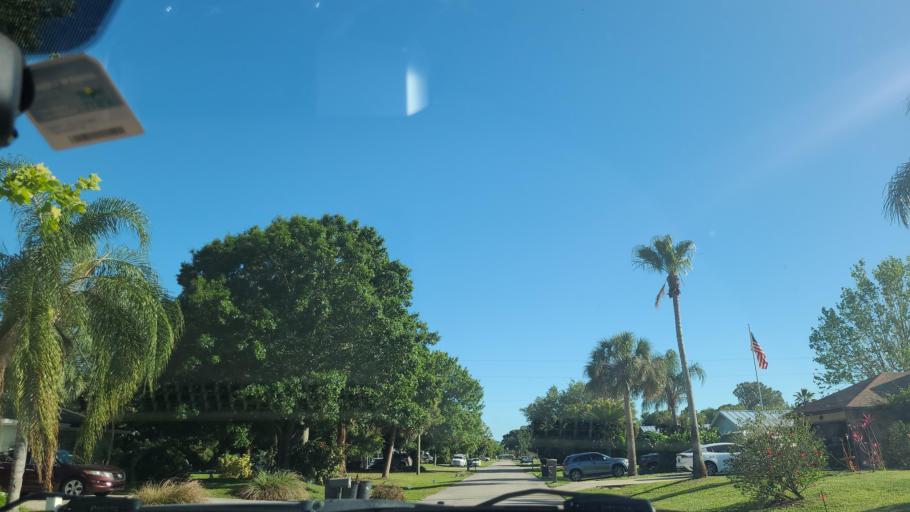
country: US
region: Florida
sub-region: Indian River County
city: Sebastian
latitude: 27.8034
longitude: -80.4855
